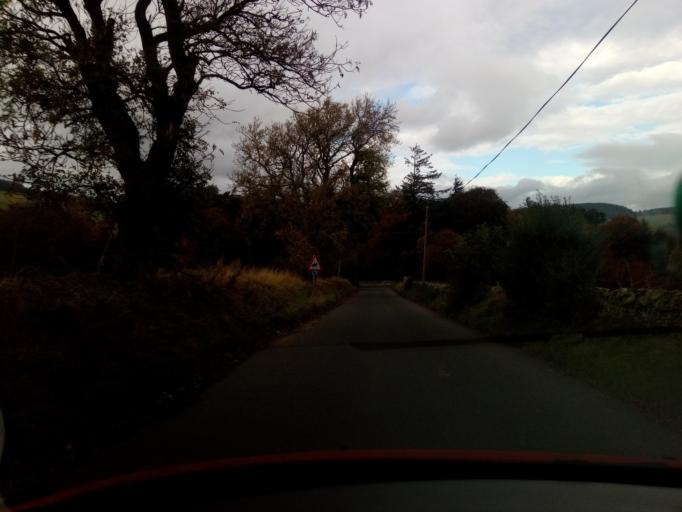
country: GB
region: Scotland
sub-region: The Scottish Borders
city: Peebles
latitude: 55.6325
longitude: -3.1410
